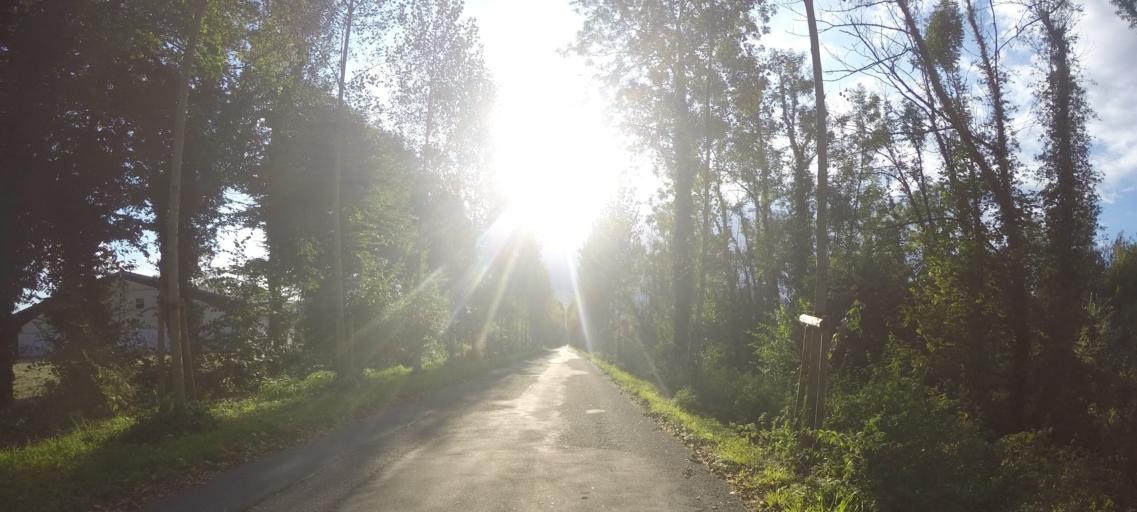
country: DE
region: North Rhine-Westphalia
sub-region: Regierungsbezirk Arnsberg
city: Lippstadt
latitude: 51.6953
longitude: 8.3399
